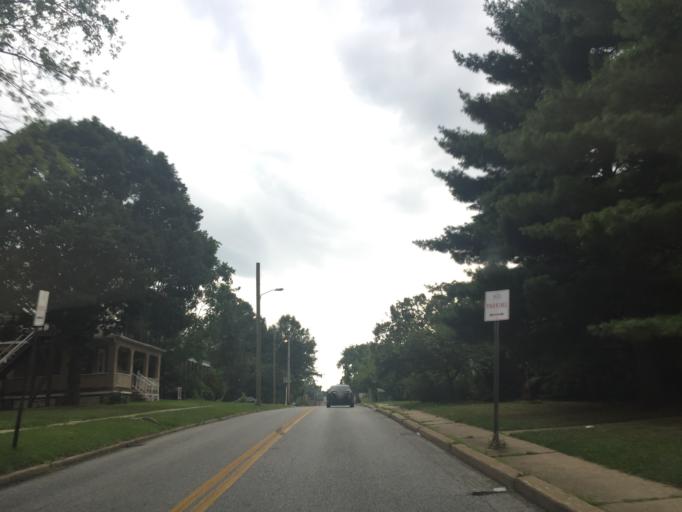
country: US
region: Maryland
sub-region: Baltimore County
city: Parkville
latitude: 39.3550
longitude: -76.5645
